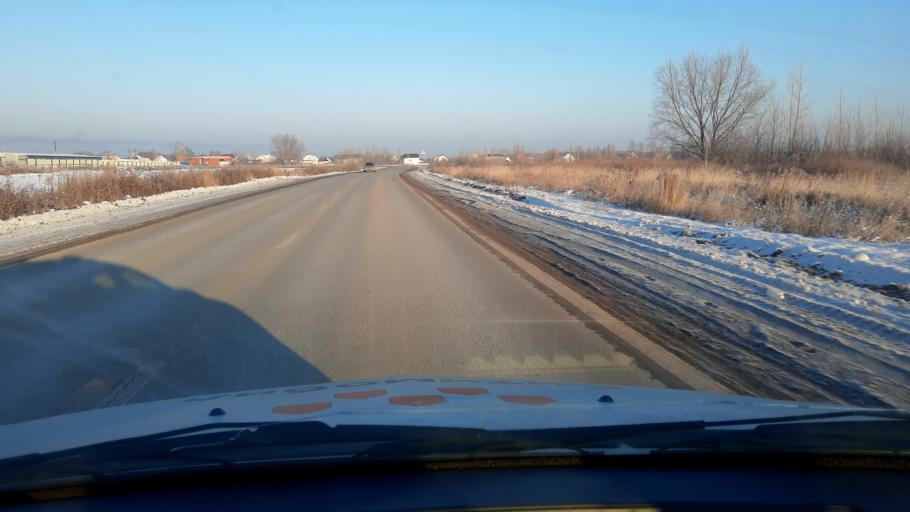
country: RU
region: Bashkortostan
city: Kabakovo
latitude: 54.7408
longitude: 56.2030
